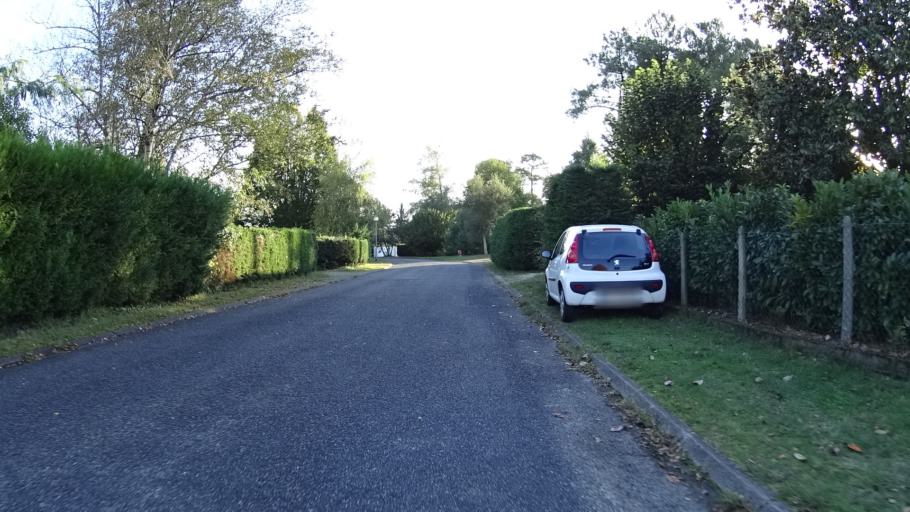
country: FR
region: Aquitaine
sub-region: Departement des Landes
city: Saint-Paul-les-Dax
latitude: 43.7408
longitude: -1.0480
